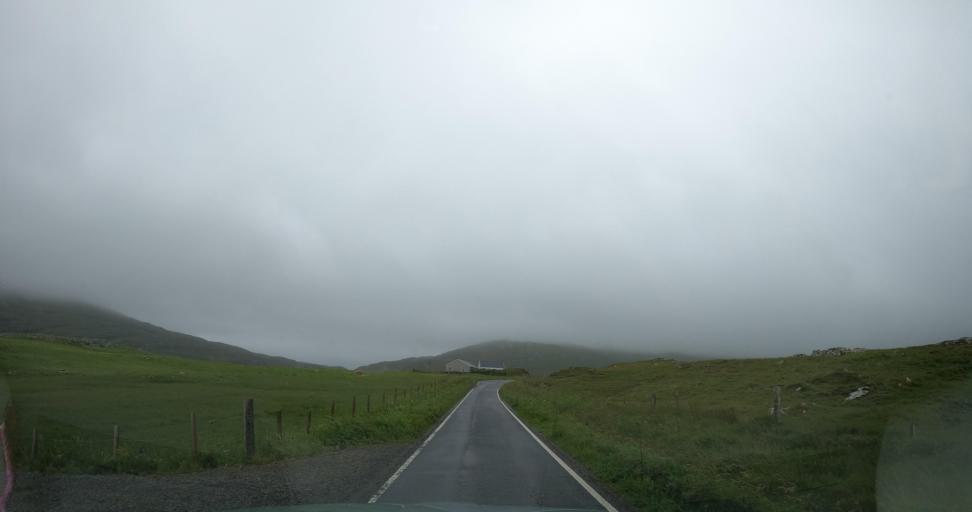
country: GB
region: Scotland
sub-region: Eilean Siar
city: Barra
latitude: 57.0022
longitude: -7.4892
